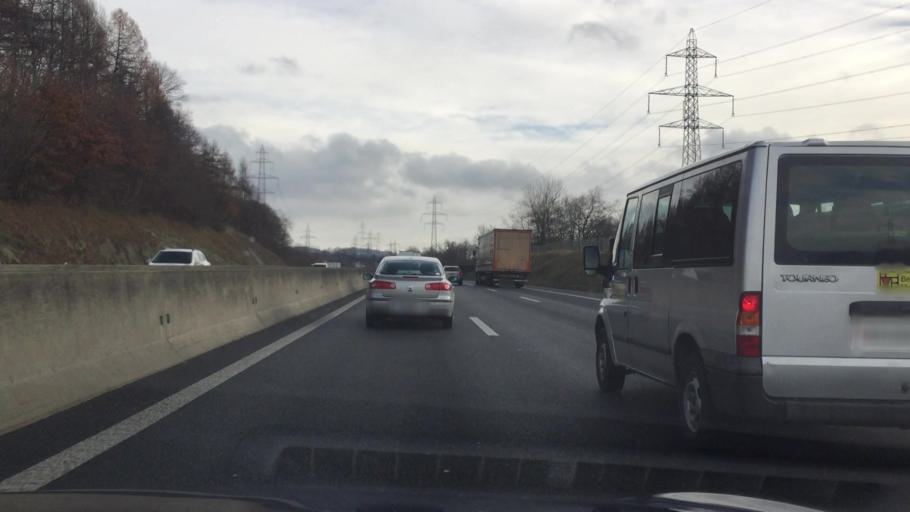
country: CH
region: Vaud
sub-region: Ouest Lausannois District
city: Crissier
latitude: 46.5626
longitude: 6.5797
